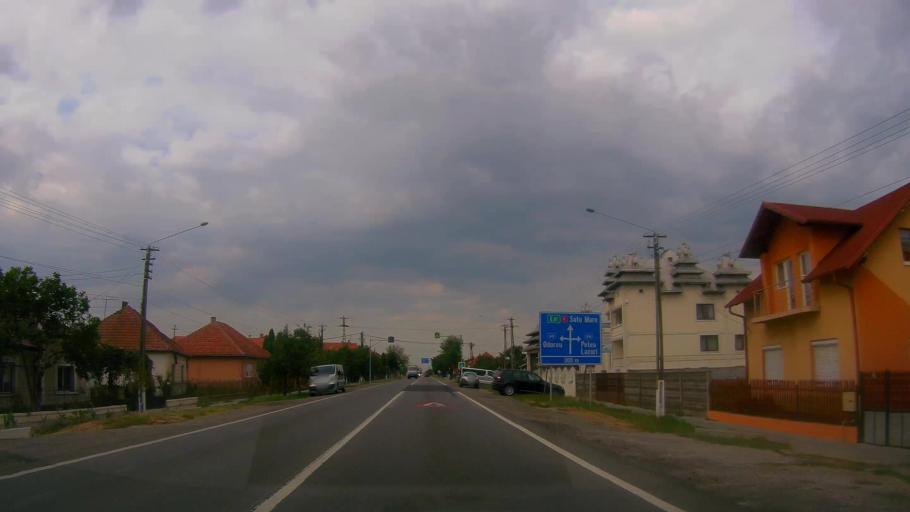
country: RO
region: Satu Mare
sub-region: Comuna Botiz
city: Botiz
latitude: 47.8287
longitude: 22.9516
